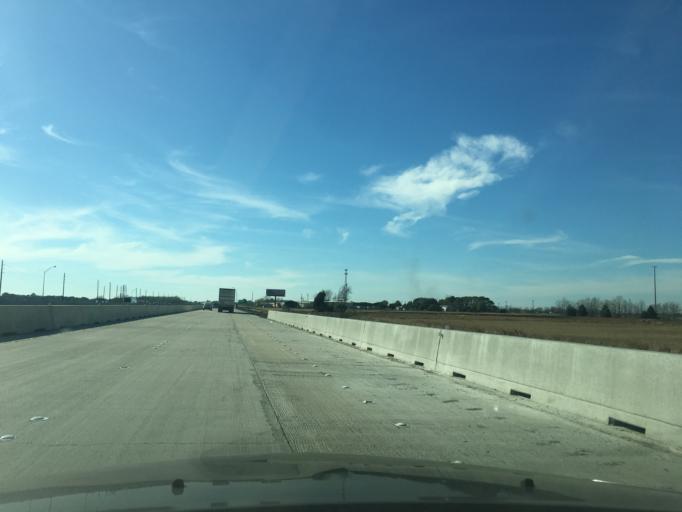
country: US
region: Texas
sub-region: Fort Bend County
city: Pleak
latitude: 29.4895
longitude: -95.9237
